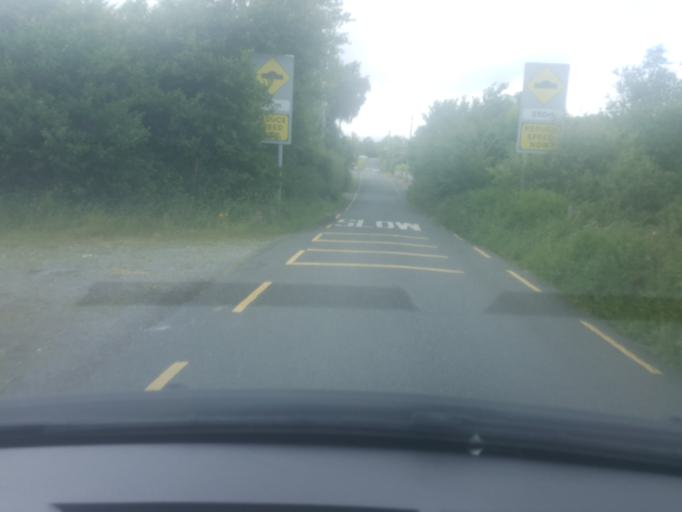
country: IE
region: Munster
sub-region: Ciarrai
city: Cill Airne
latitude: 52.1043
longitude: -9.5059
